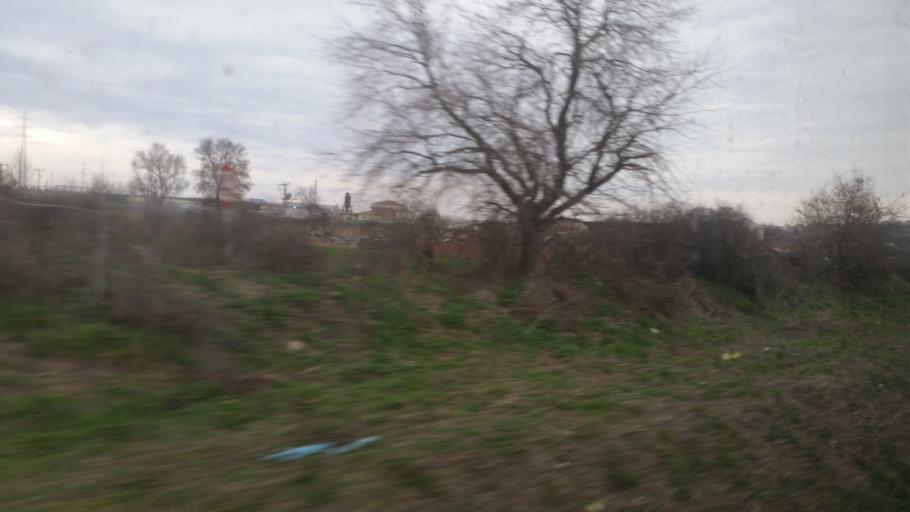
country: TR
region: Tekirdag
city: Velimese
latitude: 41.2563
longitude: 27.9115
